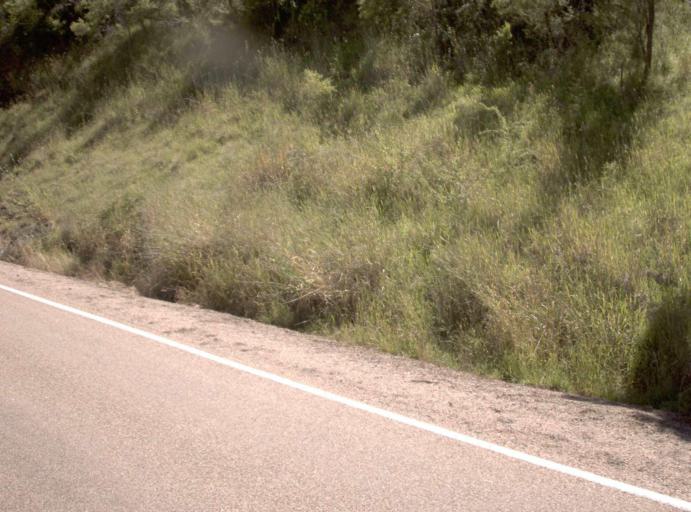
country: AU
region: Victoria
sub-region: East Gippsland
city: Lakes Entrance
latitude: -37.4885
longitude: 148.1870
